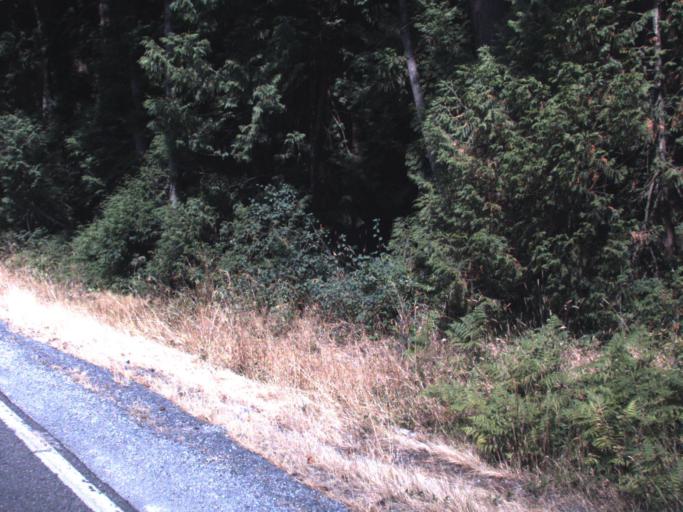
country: US
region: Washington
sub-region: Snohomish County
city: North Creek
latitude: 47.8098
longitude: -122.1680
